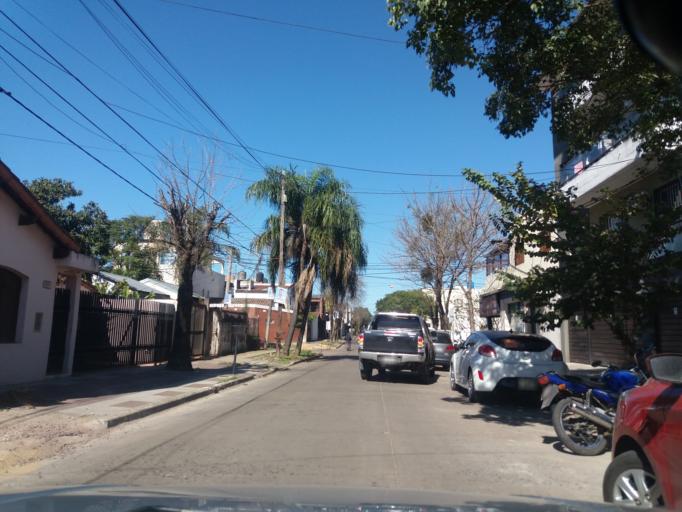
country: AR
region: Corrientes
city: Corrientes
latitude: -27.4734
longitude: -58.8195
